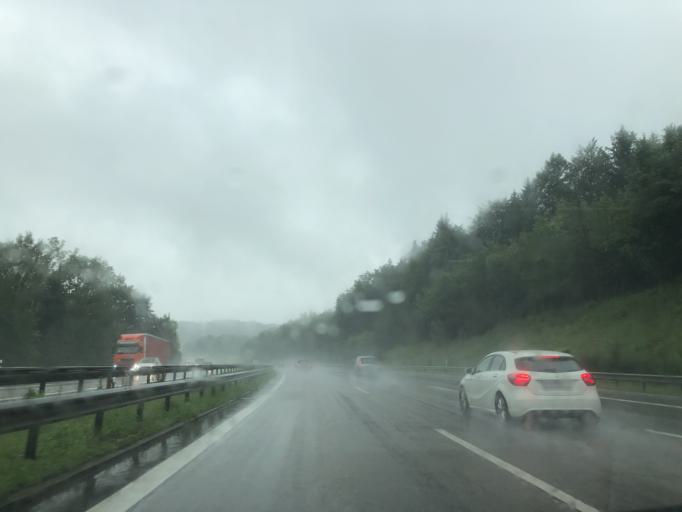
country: DE
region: Bavaria
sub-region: Upper Bavaria
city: Vagen
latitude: 47.8395
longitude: 11.8719
